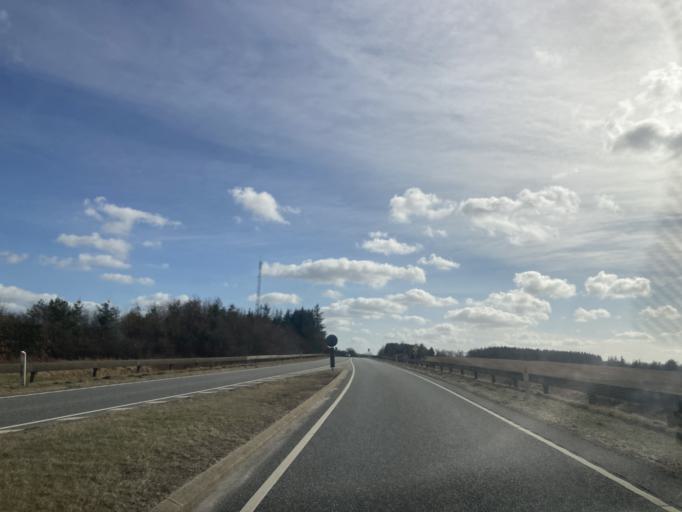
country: DK
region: Central Jutland
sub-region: Hedensted Kommune
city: Torring
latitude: 55.9889
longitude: 9.3890
